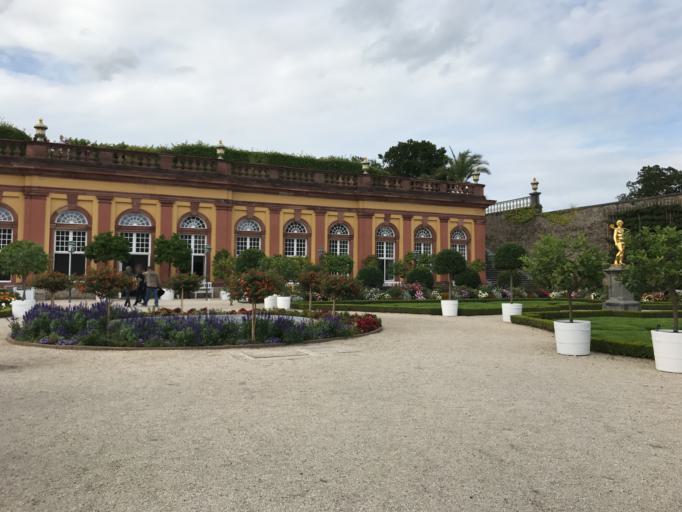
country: DE
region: Hesse
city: Weilburg
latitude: 50.4840
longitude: 8.2631
